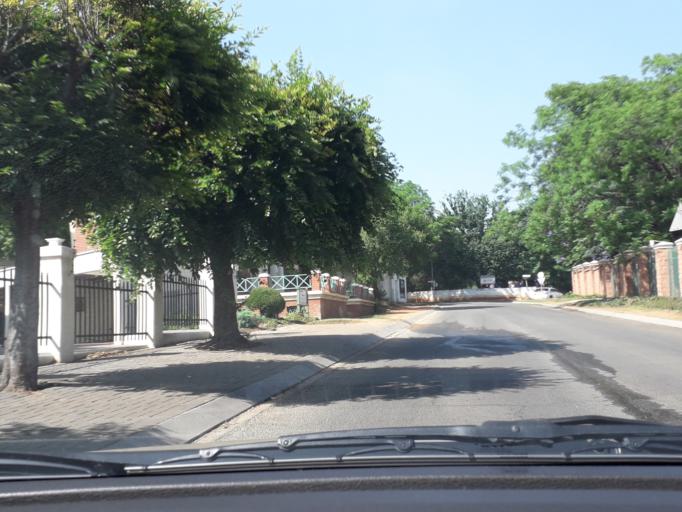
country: ZA
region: Gauteng
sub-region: City of Johannesburg Metropolitan Municipality
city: Midrand
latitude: -26.0457
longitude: 28.0587
